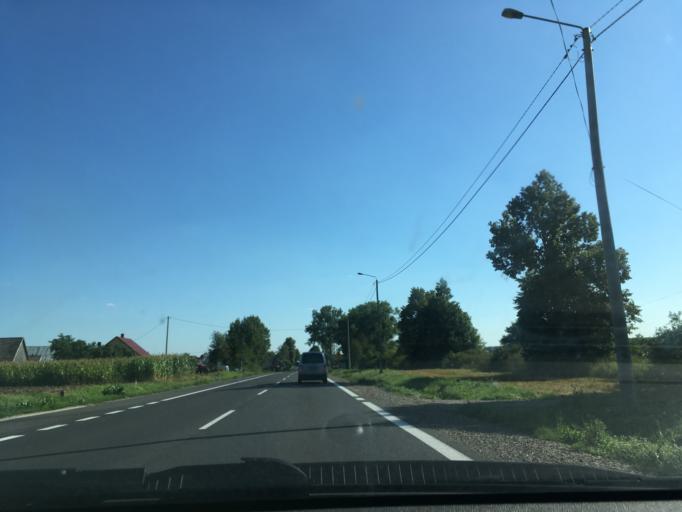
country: PL
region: Podlasie
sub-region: Powiat sokolski
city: Suchowola
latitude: 53.4641
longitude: 23.0889
